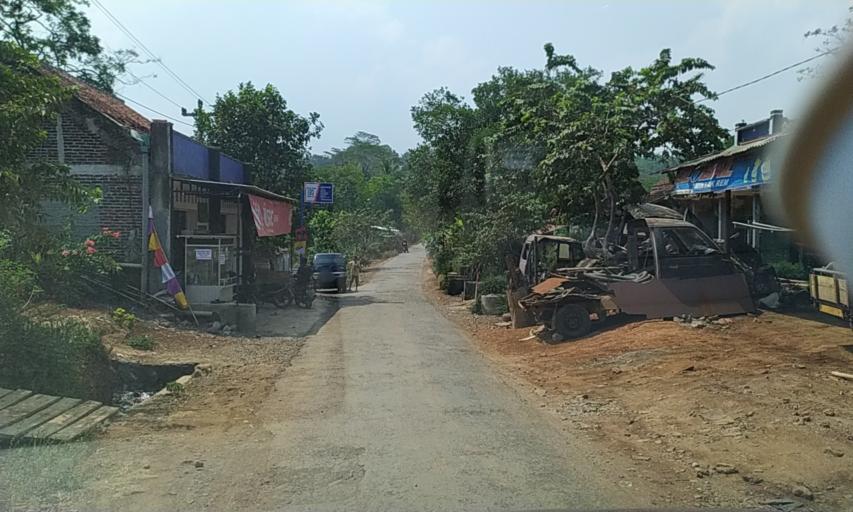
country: ID
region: Central Java
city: Karanggintung
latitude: -7.4581
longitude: 108.8566
